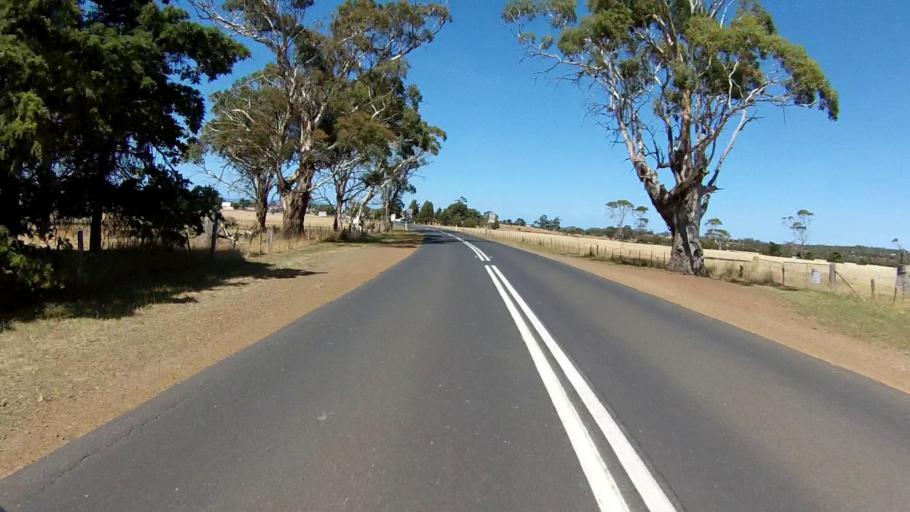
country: AU
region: Tasmania
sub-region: Break O'Day
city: St Helens
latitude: -42.1182
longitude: 148.0631
